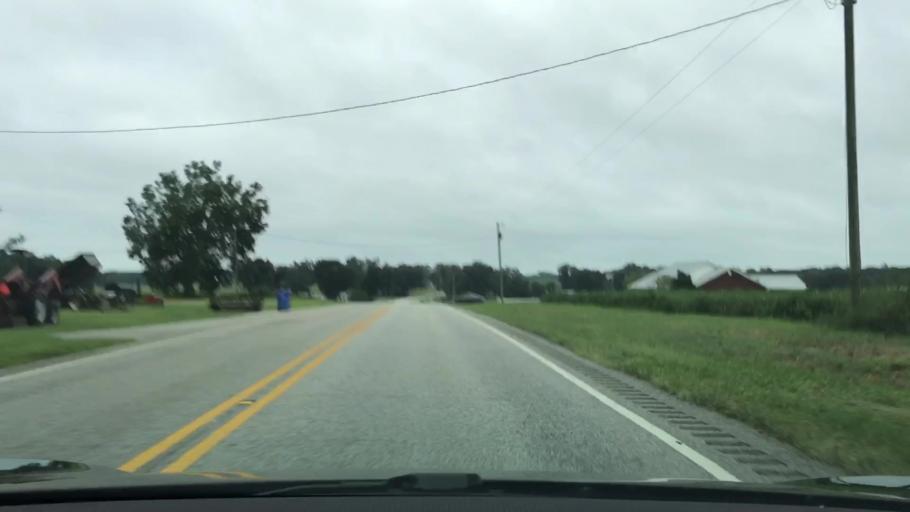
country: US
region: Alabama
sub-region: Coffee County
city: Elba
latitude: 31.3233
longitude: -86.1337
